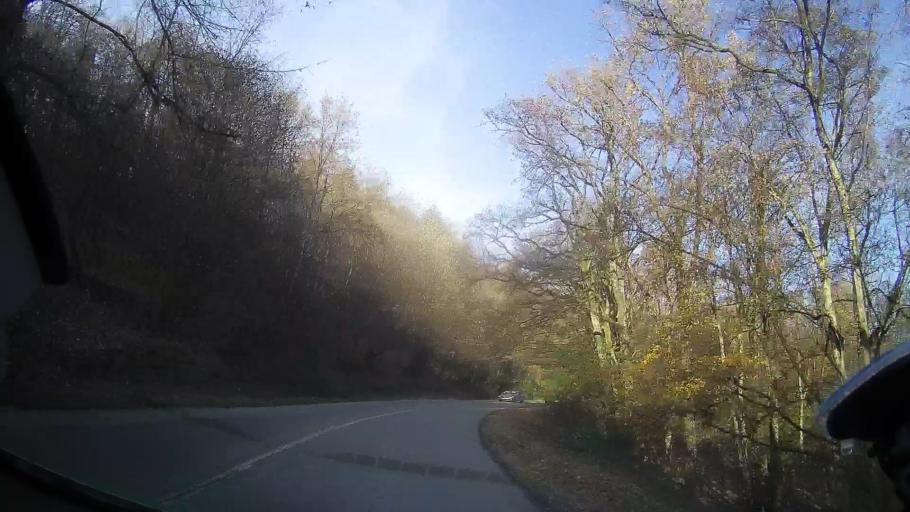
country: RO
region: Bihor
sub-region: Comuna Brusturi
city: Brusturi
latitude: 47.1041
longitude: 22.2468
